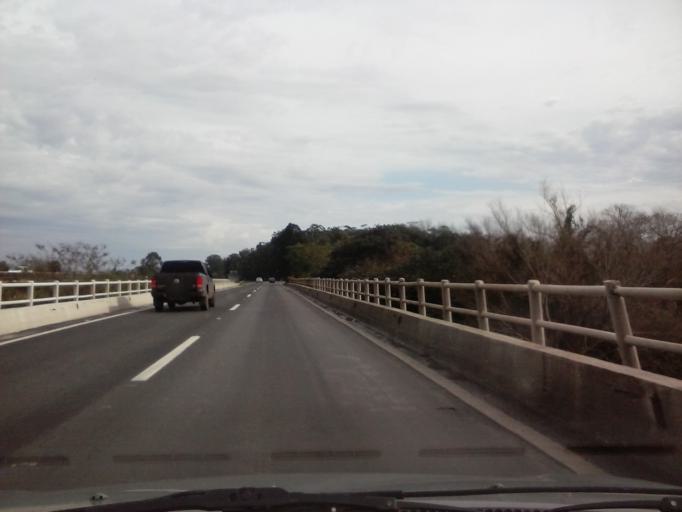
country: BR
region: Rio Grande do Sul
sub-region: Porto Alegre
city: Porto Alegre
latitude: -29.9873
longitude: -51.2396
